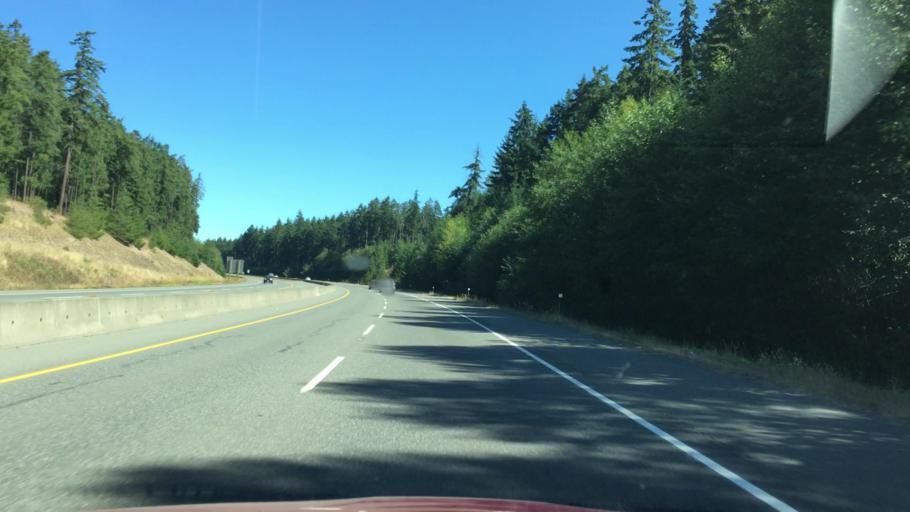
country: CA
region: British Columbia
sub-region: Regional District of Nanaimo
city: Parksville
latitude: 49.3201
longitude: -124.4064
